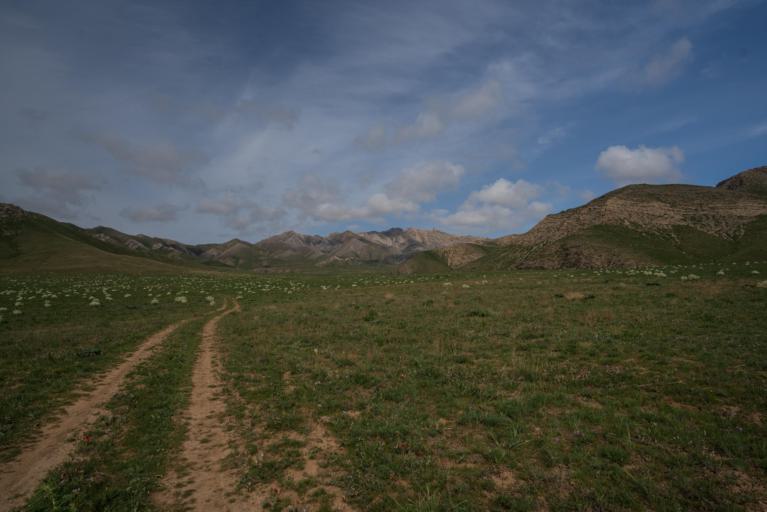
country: KZ
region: Ongtustik Qazaqstan
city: Ashchysay
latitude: 43.7309
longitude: 68.8353
